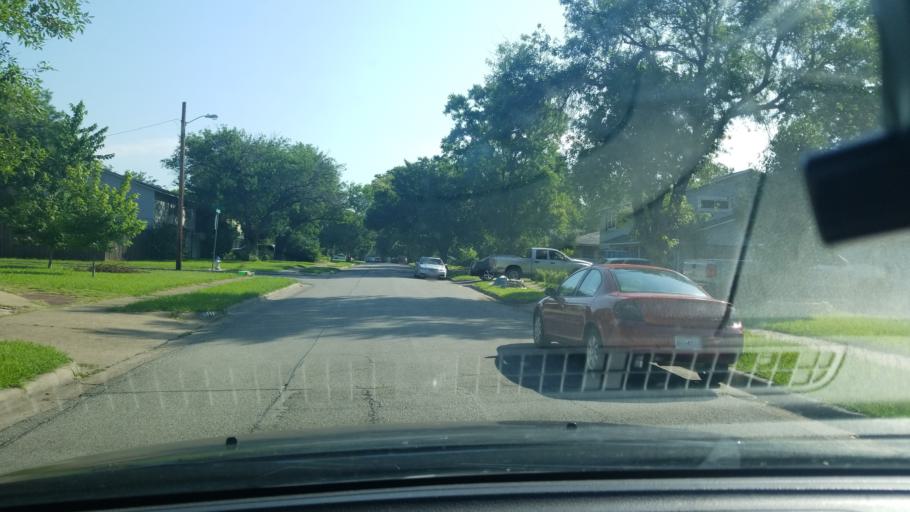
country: US
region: Texas
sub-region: Dallas County
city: Mesquite
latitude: 32.8215
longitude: -96.6396
